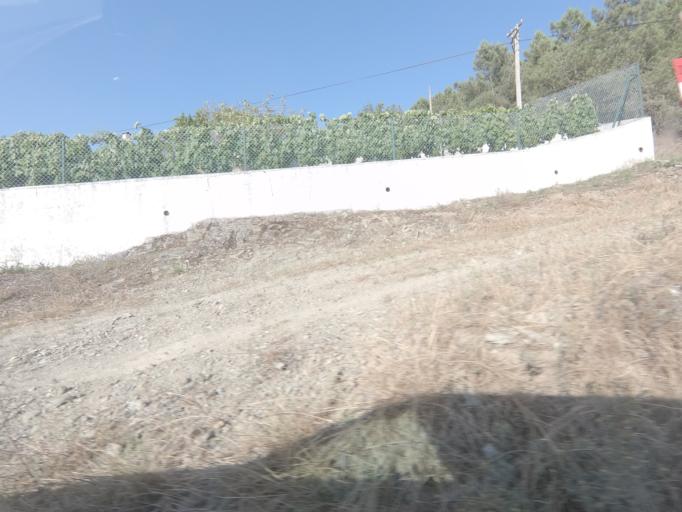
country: PT
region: Vila Real
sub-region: Sabrosa
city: Vilela
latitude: 41.1930
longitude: -7.6197
